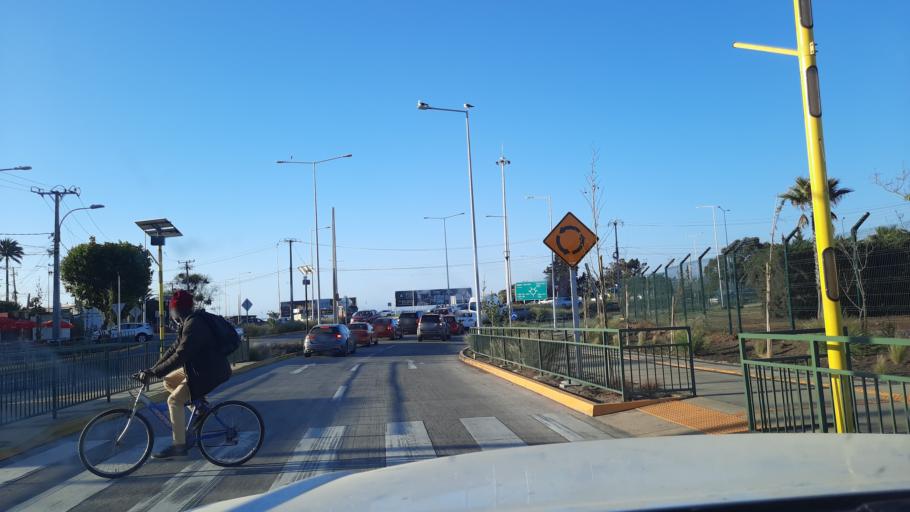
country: CL
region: Valparaiso
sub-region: Provincia de Valparaiso
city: Vina del Mar
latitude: -32.9225
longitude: -71.5068
